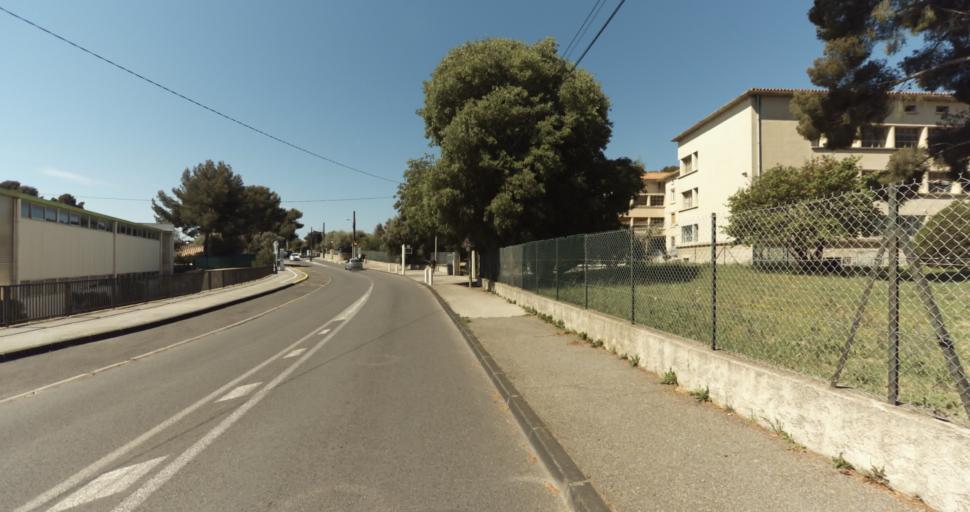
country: FR
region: Provence-Alpes-Cote d'Azur
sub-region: Departement du Var
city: Le Revest-les-Eaux
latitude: 43.1447
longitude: 5.8963
